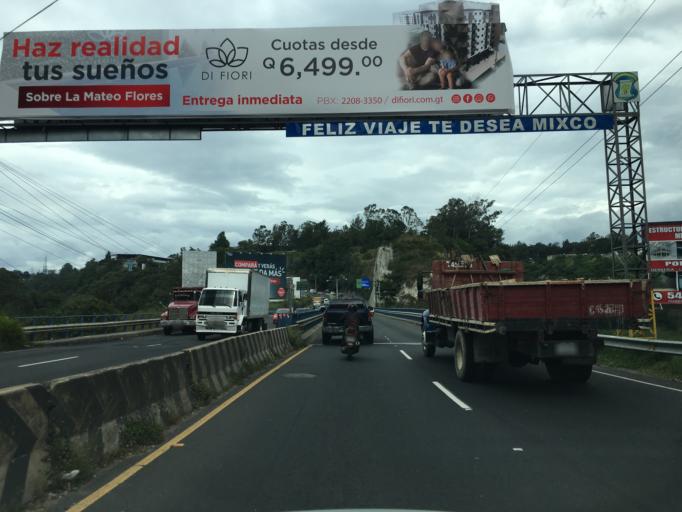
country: GT
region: Guatemala
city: Mixco
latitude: 14.5921
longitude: -90.5741
